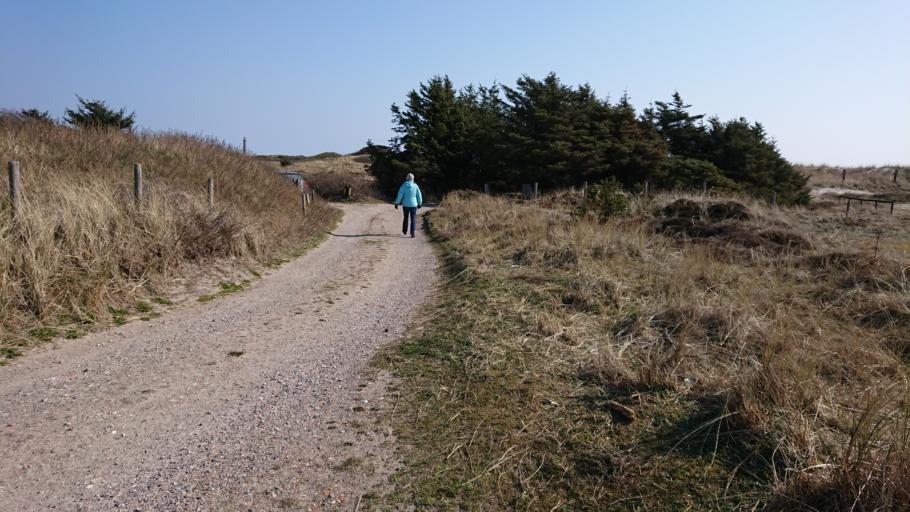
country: DK
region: North Denmark
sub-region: Frederikshavn Kommune
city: Skagen
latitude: 57.7287
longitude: 10.6125
